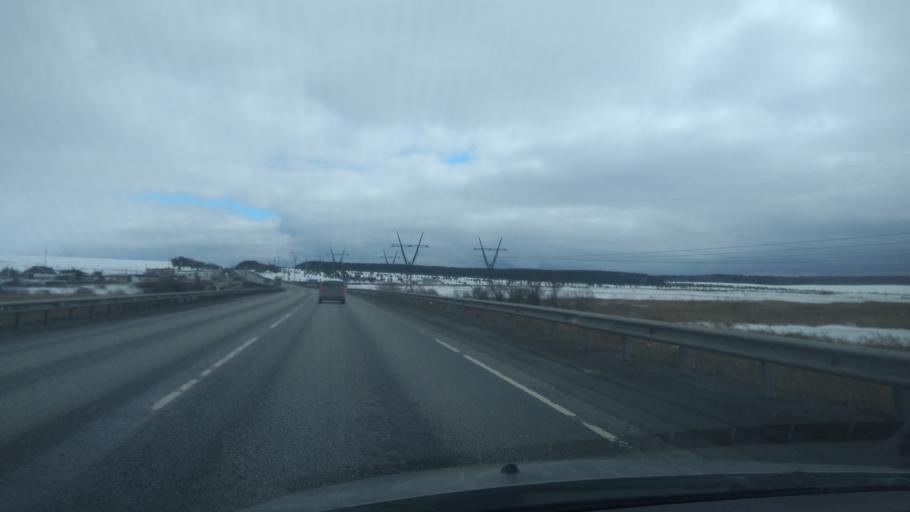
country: RU
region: Sverdlovsk
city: Achit
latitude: 56.7834
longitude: 57.8989
